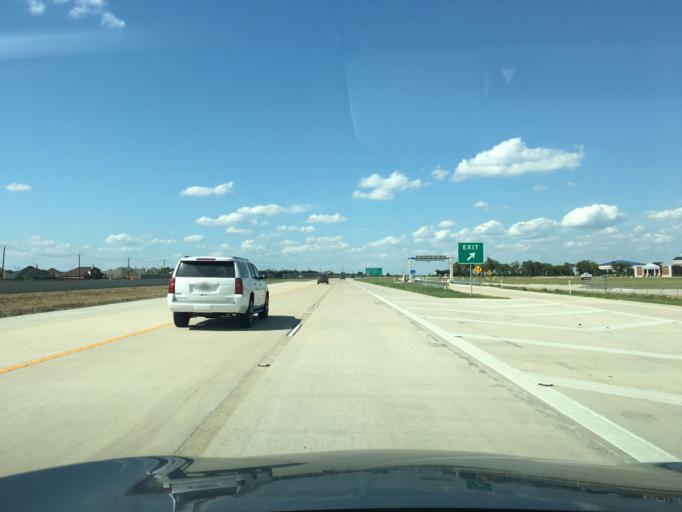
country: US
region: Texas
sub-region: Tarrant County
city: Mansfield
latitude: 32.6120
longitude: -97.0765
